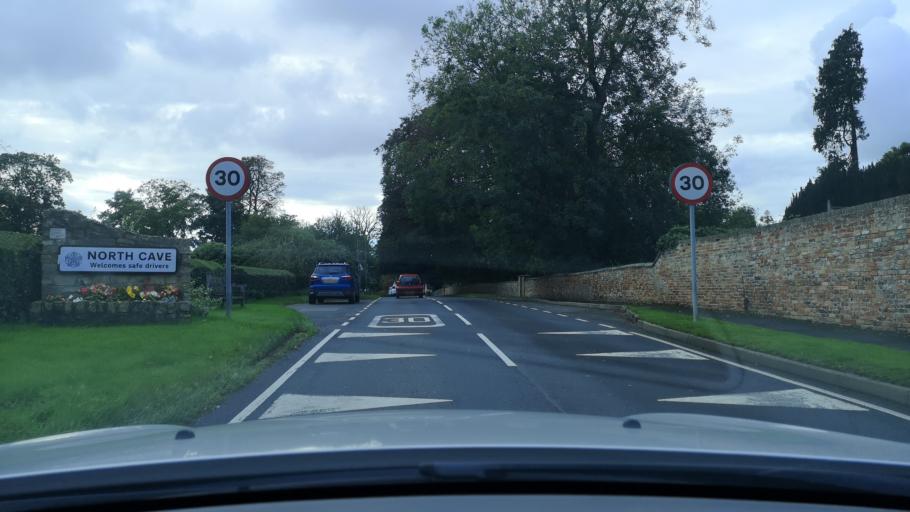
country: GB
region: England
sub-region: East Riding of Yorkshire
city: North Cave
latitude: 53.7830
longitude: -0.6385
